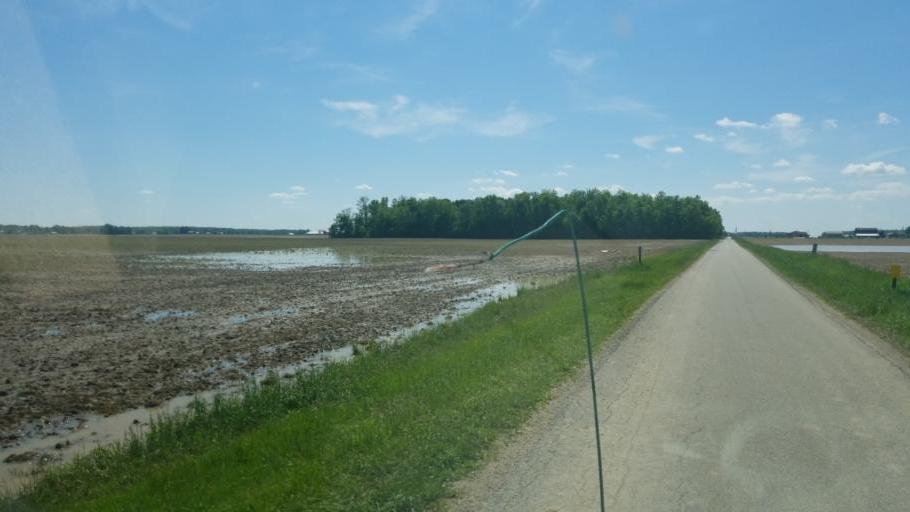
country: US
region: Ohio
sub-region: Crawford County
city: Bucyrus
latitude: 40.9795
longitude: -83.0019
